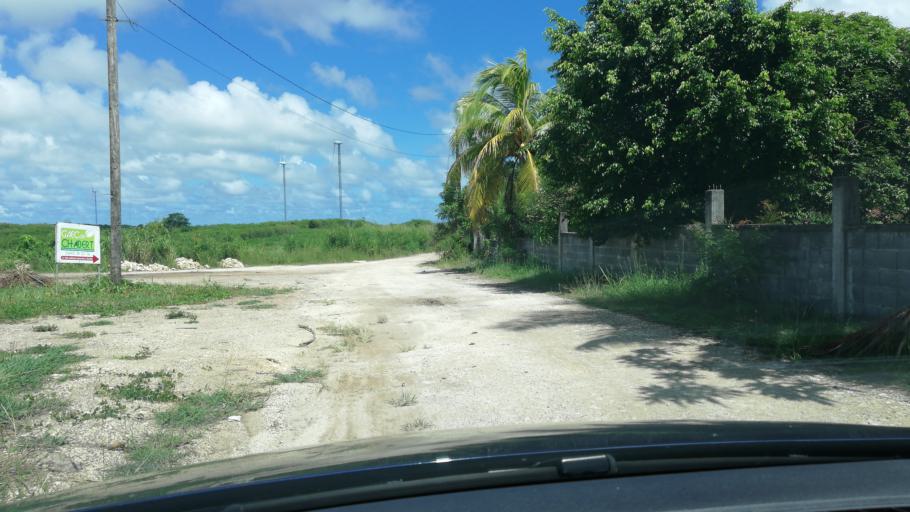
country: GP
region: Guadeloupe
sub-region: Guadeloupe
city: Petit-Canal
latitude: 16.3805
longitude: -61.4314
